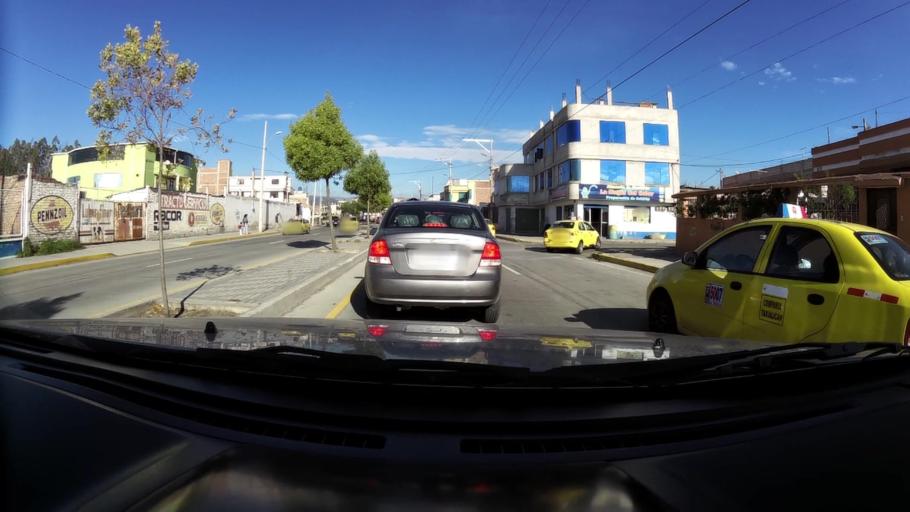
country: EC
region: Chimborazo
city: Riobamba
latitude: -1.6864
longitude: -78.6420
